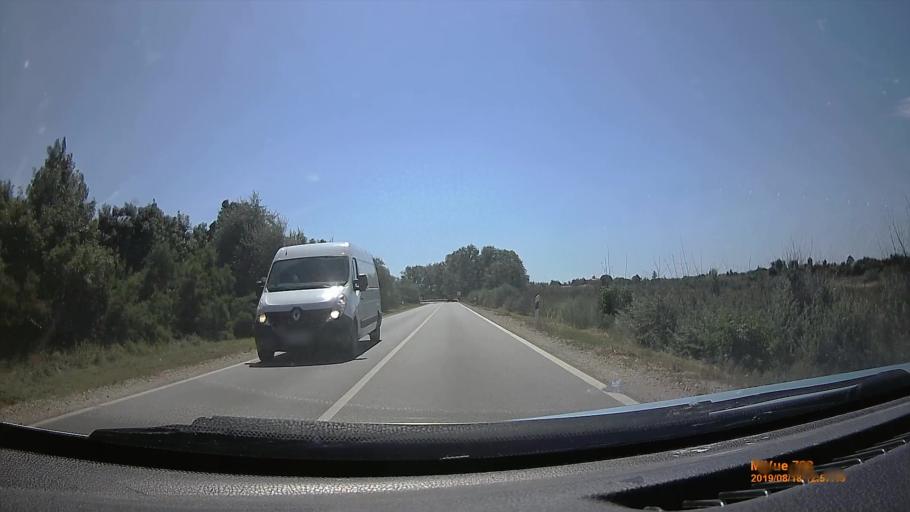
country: HU
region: Fejer
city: Sarkeresztur
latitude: 47.0148
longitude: 18.5446
